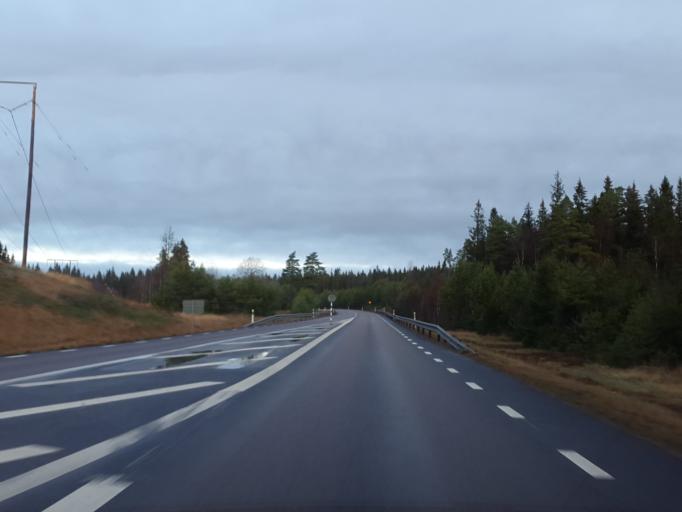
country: SE
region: Vaestra Goetaland
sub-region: Boras Kommun
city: Sandared
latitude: 57.7905
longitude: 12.7709
